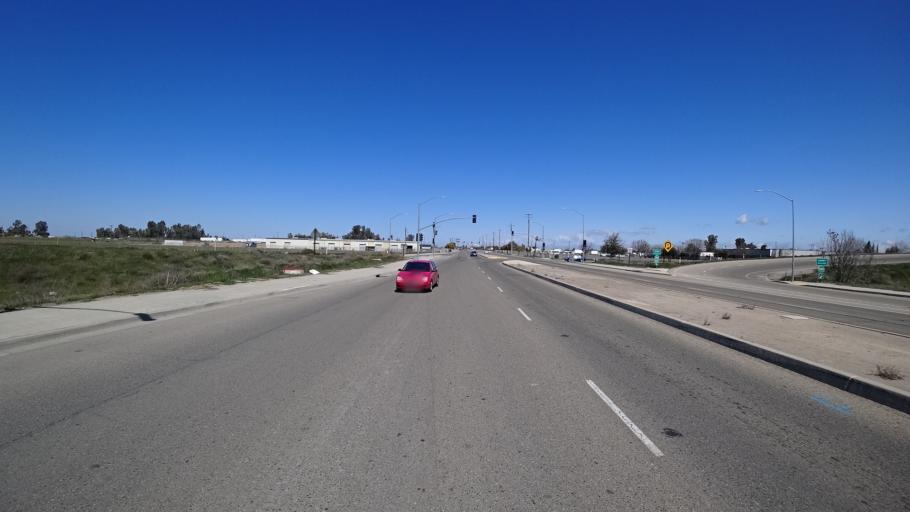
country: US
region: California
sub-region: Fresno County
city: West Park
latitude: 36.7389
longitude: -119.8445
